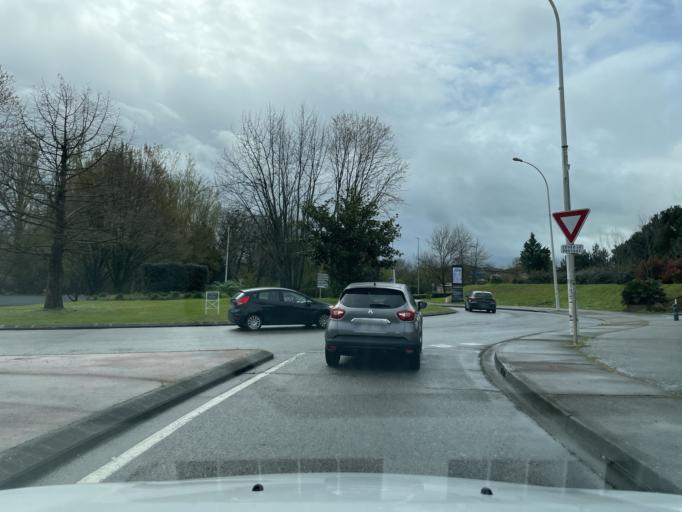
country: FR
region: Midi-Pyrenees
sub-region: Departement de la Haute-Garonne
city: Tournefeuille
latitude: 43.5788
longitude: 1.3520
